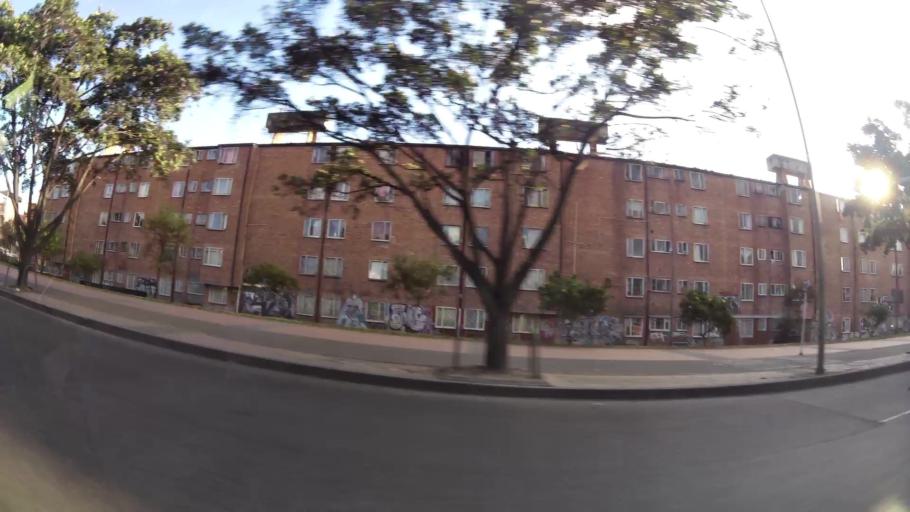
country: CO
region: Cundinamarca
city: Soacha
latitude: 4.5690
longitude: -74.1466
